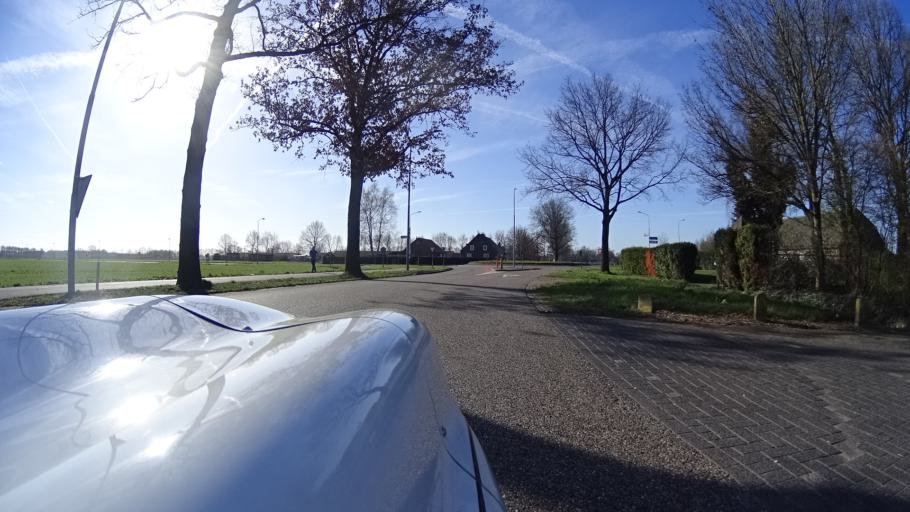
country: NL
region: North Brabant
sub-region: Gemeente Uden
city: Volkel
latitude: 51.6460
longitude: 5.6731
